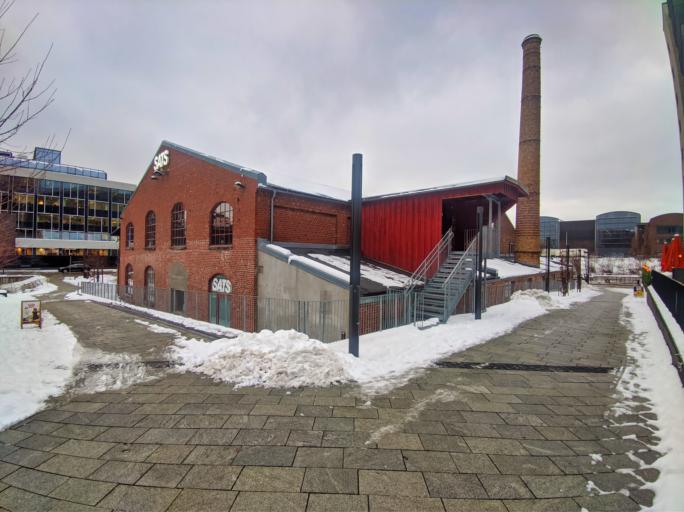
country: NO
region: Oslo
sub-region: Oslo
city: Oslo
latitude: 59.9477
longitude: 10.7720
